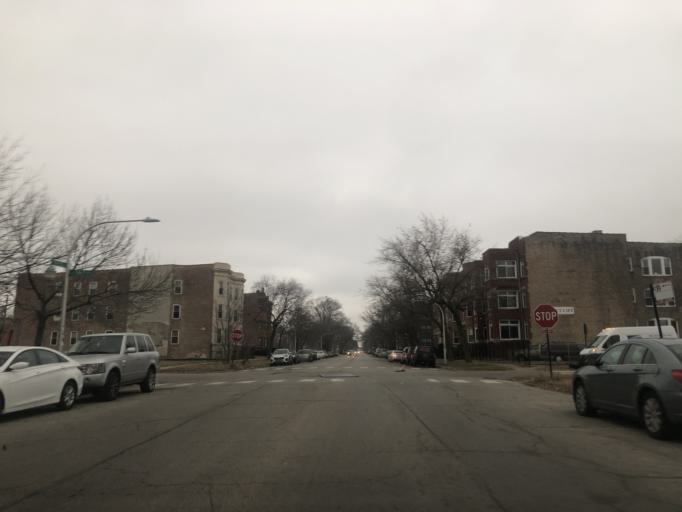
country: US
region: Illinois
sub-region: Cook County
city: Chicago
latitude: 41.7934
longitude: -87.6192
